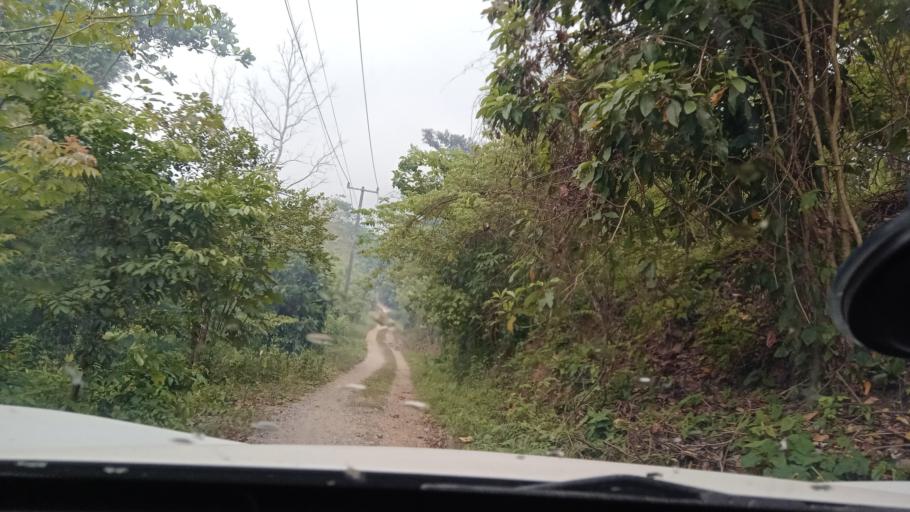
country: MX
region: Veracruz
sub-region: Uxpanapa
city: Poblado 10
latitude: 17.4507
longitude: -94.0913
